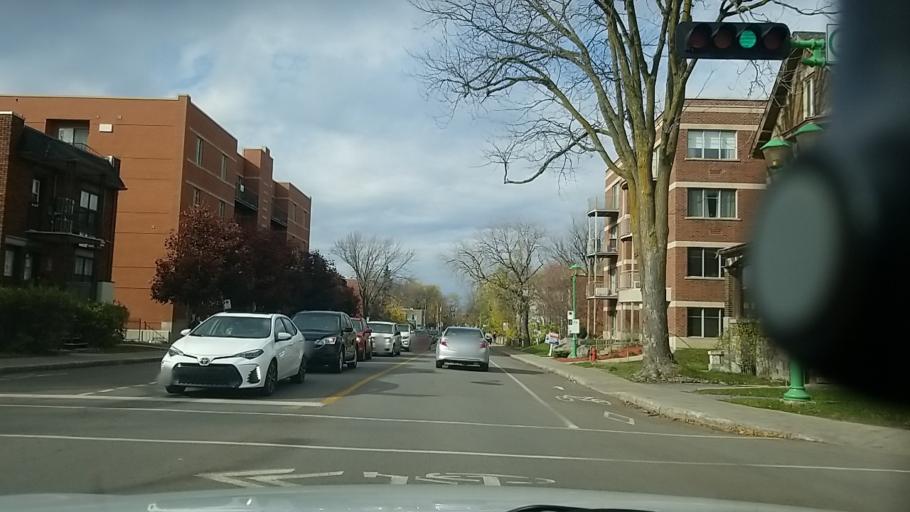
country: CA
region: Quebec
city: Saint-Laurent
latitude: 45.5150
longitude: -73.6778
